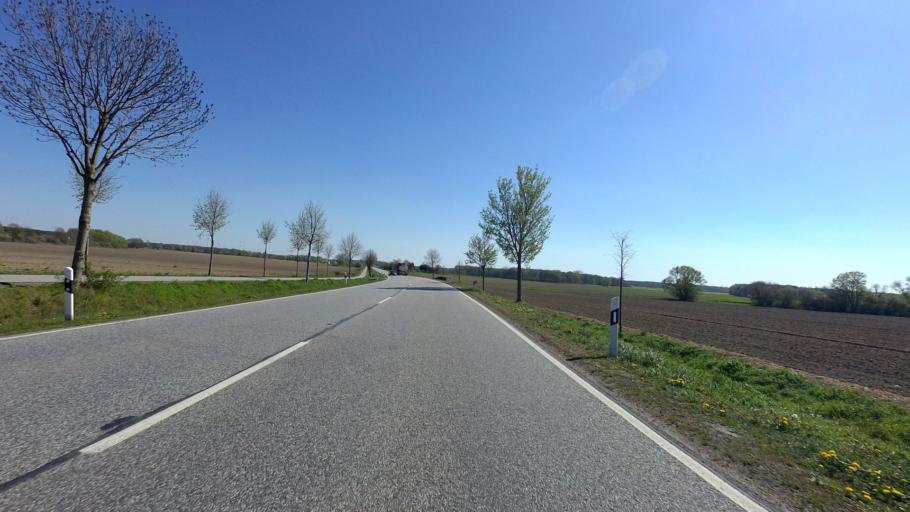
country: DE
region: Saxony-Anhalt
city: Pretzier
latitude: 52.8101
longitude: 11.2207
